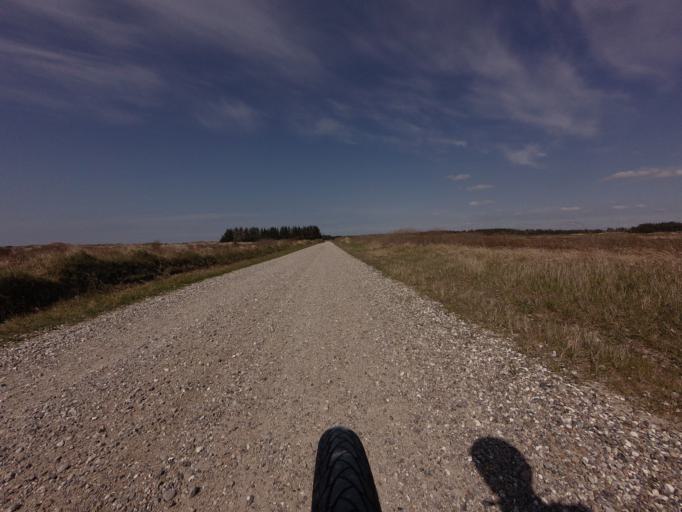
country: DK
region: North Denmark
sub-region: Jammerbugt Kommune
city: Brovst
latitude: 57.2102
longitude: 9.5535
